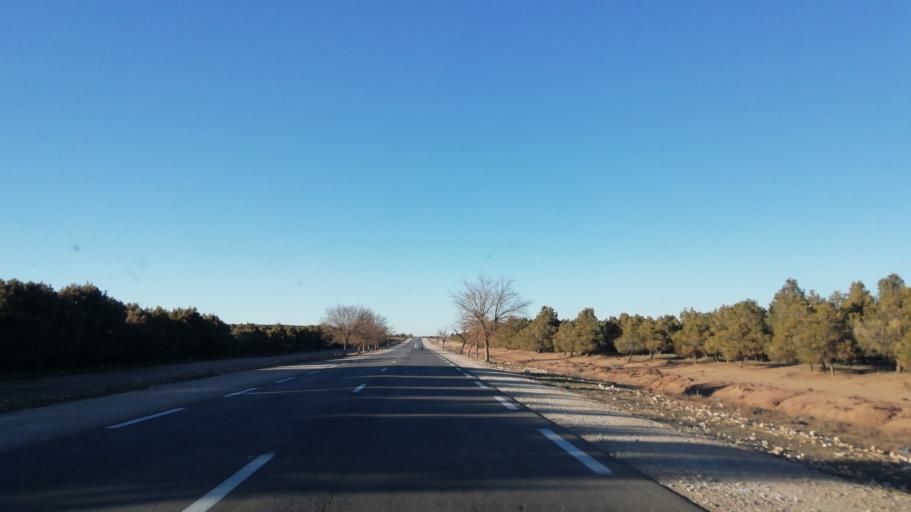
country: DZ
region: Tlemcen
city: Sebdou
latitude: 34.5121
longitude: -1.2838
